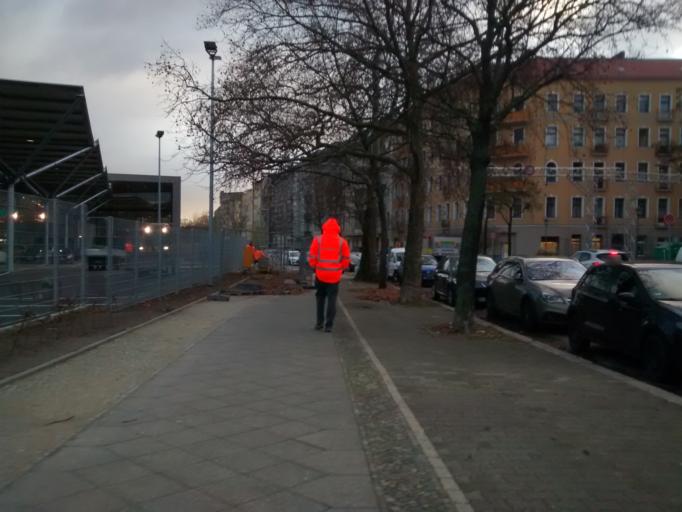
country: DE
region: Berlin
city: Moabit
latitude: 52.5328
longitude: 13.3313
